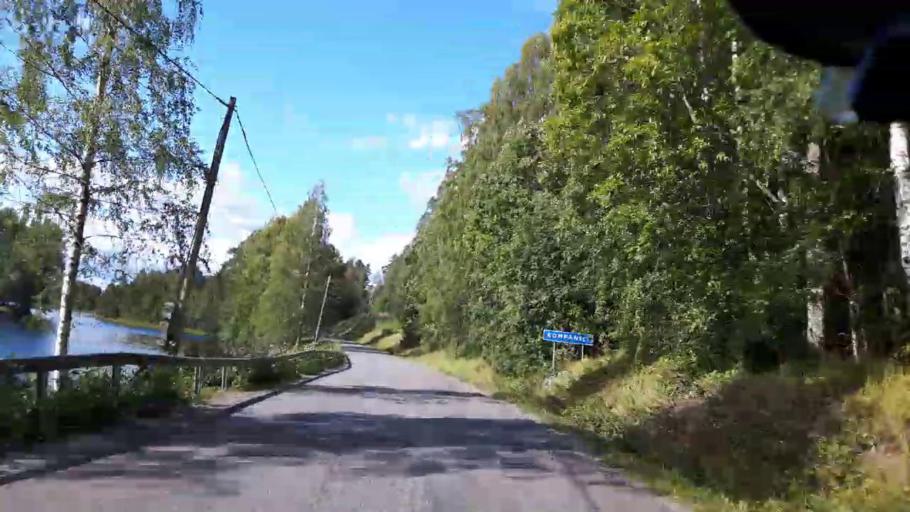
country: SE
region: Jaemtland
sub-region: Braecke Kommun
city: Braecke
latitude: 63.1773
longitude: 15.5599
